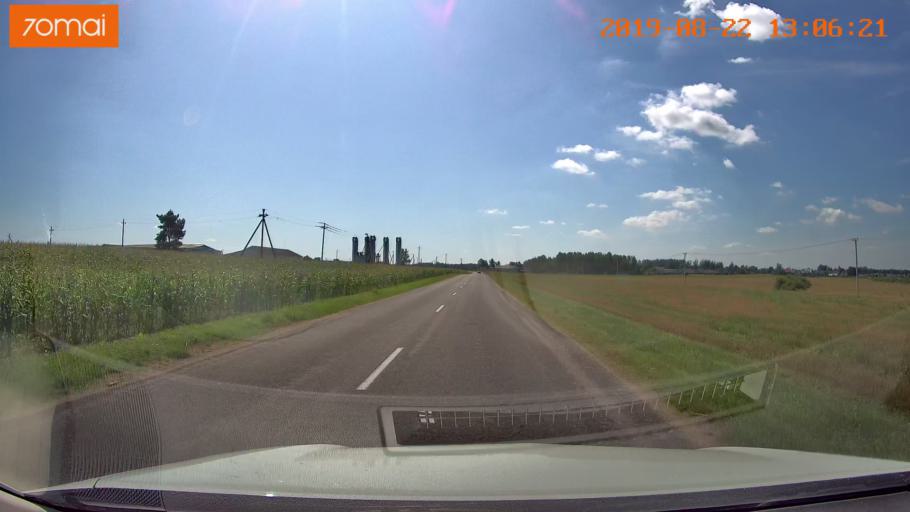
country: BY
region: Minsk
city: Prawdzinski
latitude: 53.3480
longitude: 27.8390
